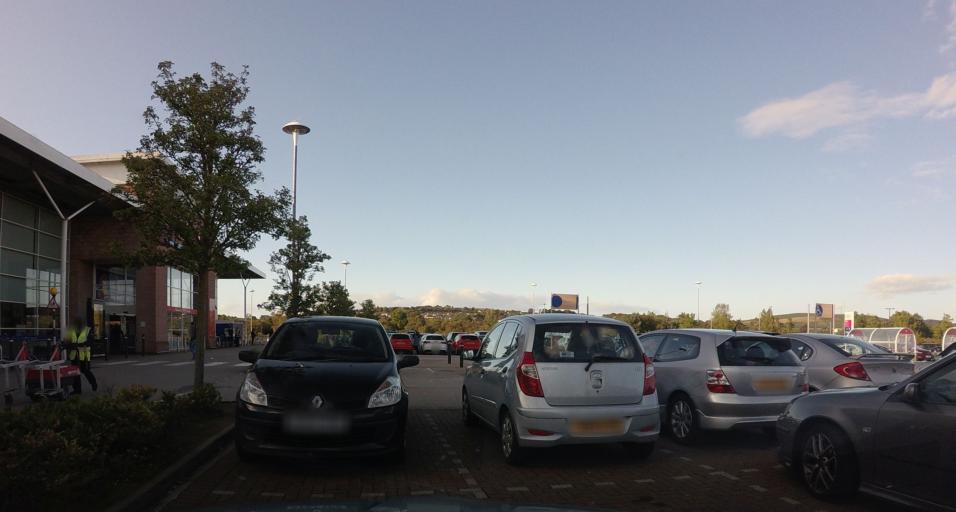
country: GB
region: Scotland
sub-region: Aberdeenshire
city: Westhill
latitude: 57.1494
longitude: -2.2749
